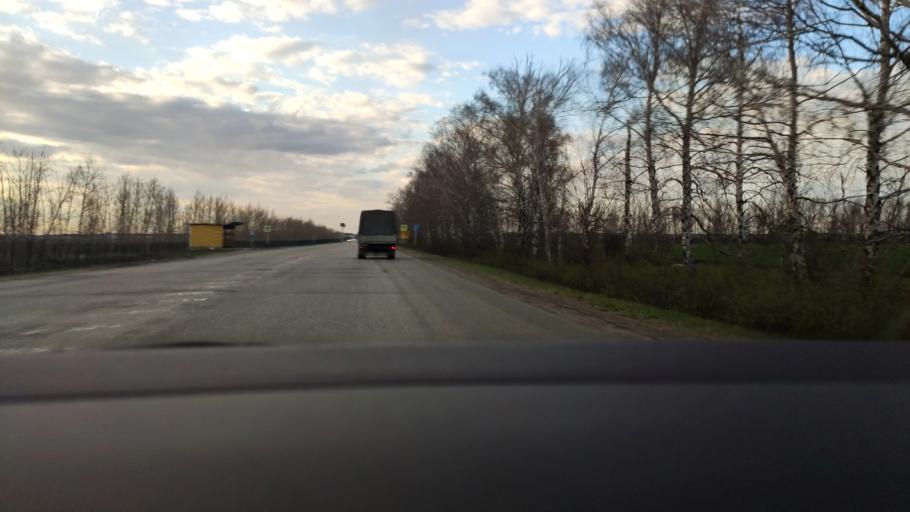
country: RU
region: Voronezj
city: Maslovka
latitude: 51.5268
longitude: 39.2951
